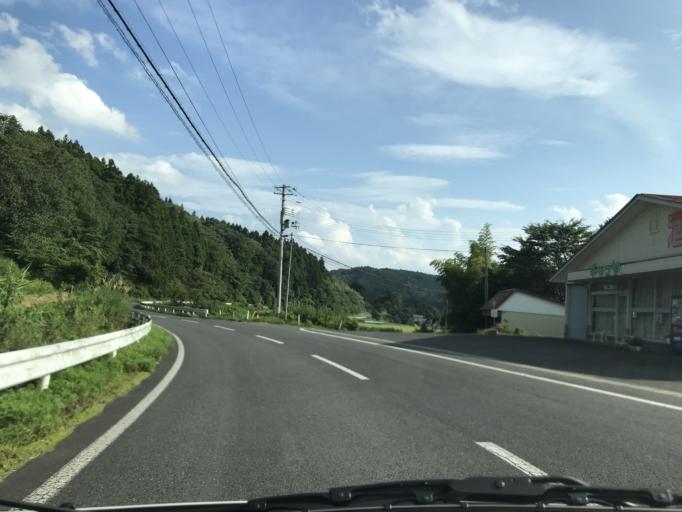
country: JP
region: Iwate
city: Ofunato
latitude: 38.9454
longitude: 141.4614
